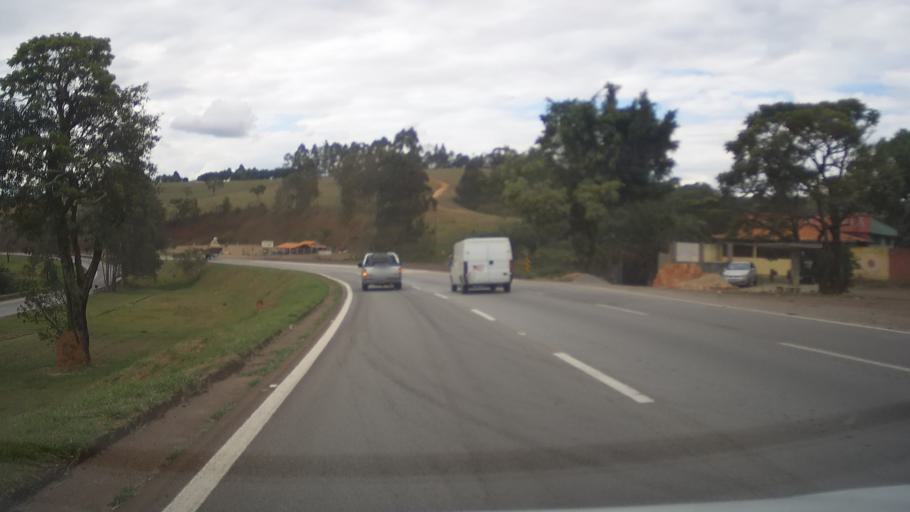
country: BR
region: Minas Gerais
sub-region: Itauna
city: Itauna
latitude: -20.3408
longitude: -44.4409
